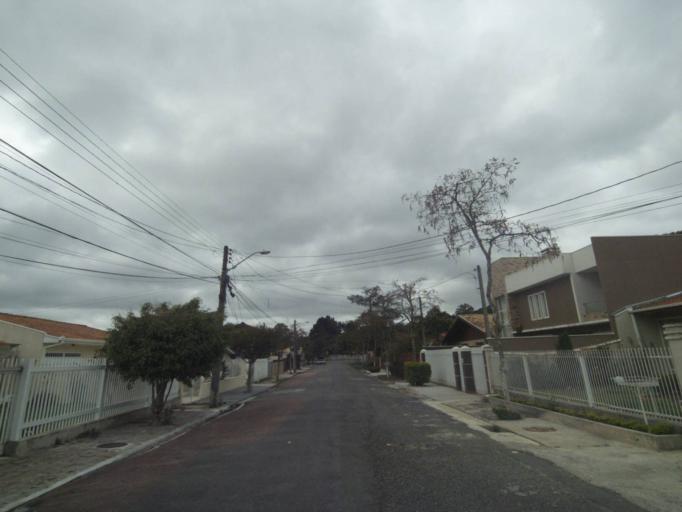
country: BR
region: Parana
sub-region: Pinhais
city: Pinhais
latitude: -25.3980
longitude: -49.2216
